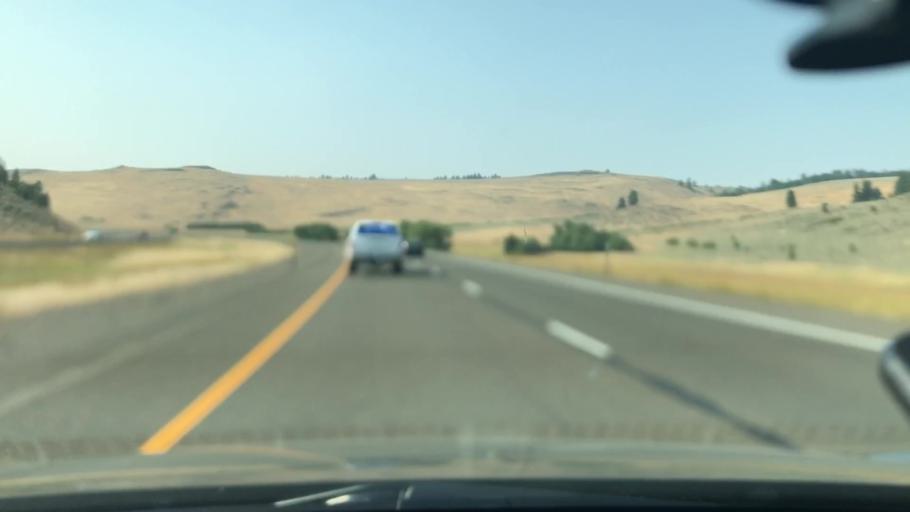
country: US
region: Oregon
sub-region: Union County
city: Union
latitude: 45.1664
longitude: -117.9647
